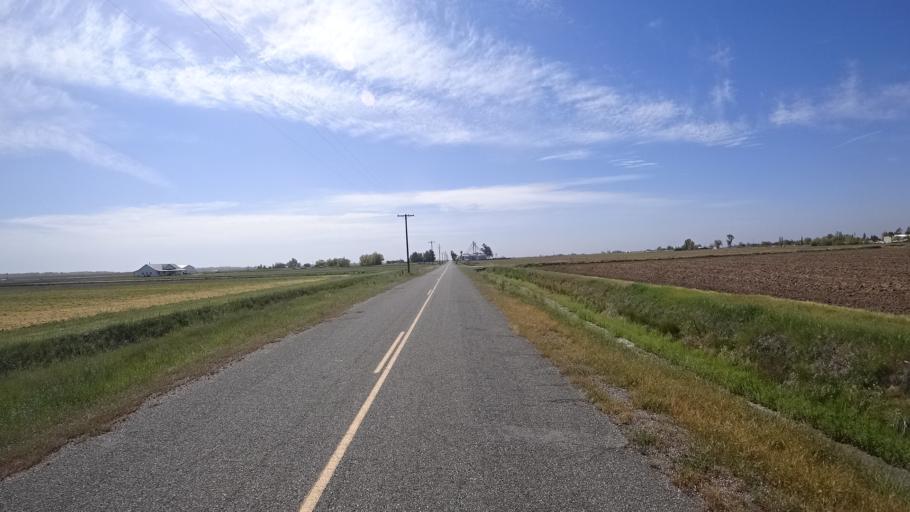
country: US
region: California
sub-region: Glenn County
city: Hamilton City
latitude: 39.5882
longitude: -122.0276
